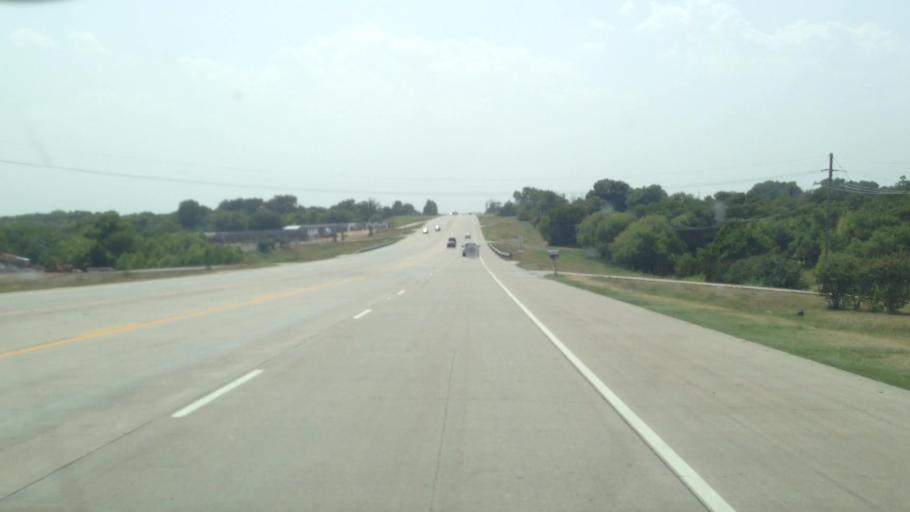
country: US
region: Texas
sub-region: Collin County
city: Farmersville
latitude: 33.1592
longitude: -96.3967
